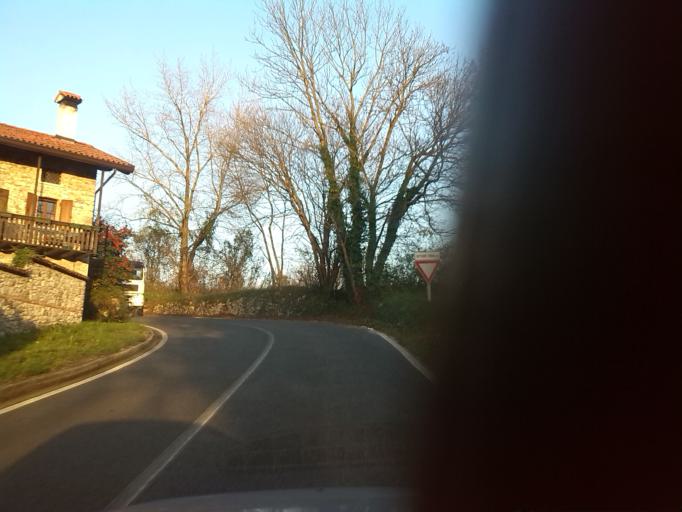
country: IT
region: Friuli Venezia Giulia
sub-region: Provincia di Udine
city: San Pietro al Natisone
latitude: 46.1105
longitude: 13.4763
